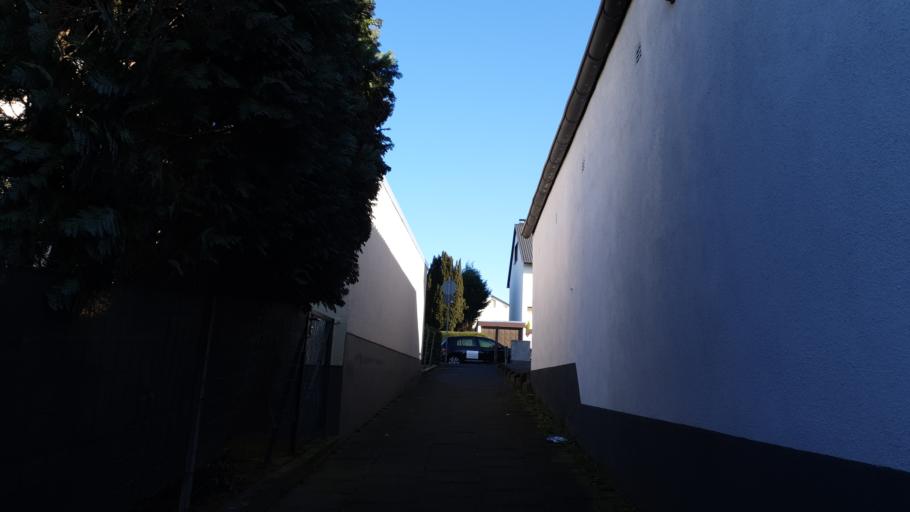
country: DE
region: North Rhine-Westphalia
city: Opladen
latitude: 51.0391
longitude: 7.0463
